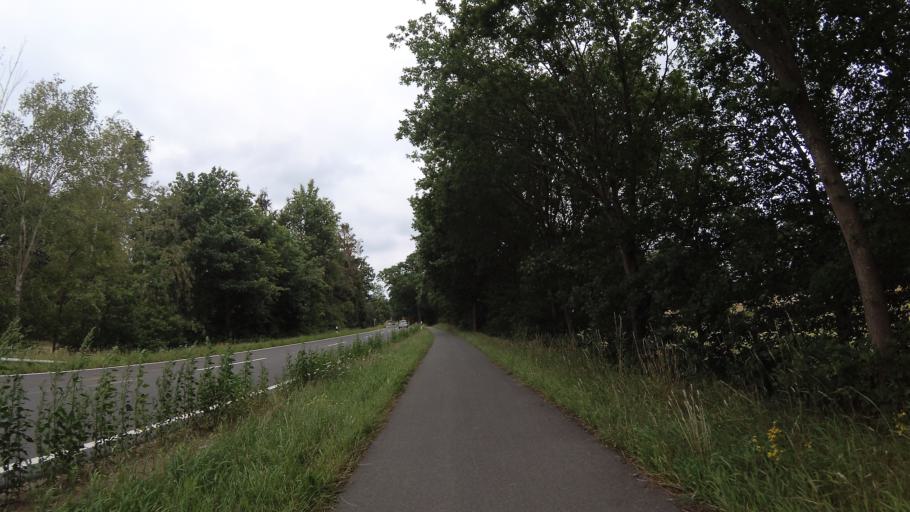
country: DE
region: Lower Saxony
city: Oberlangen
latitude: 52.8433
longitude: 7.2633
